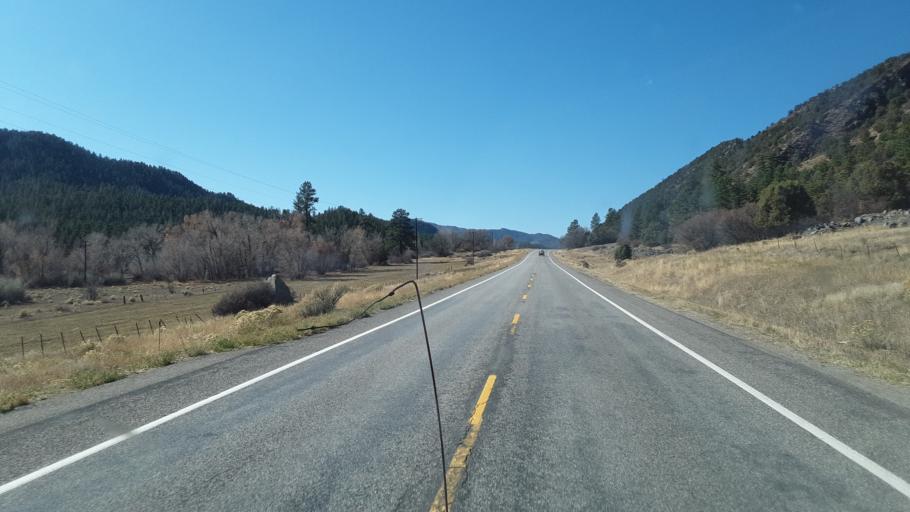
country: US
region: Colorado
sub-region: La Plata County
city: Bayfield
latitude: 37.2286
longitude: -107.3517
